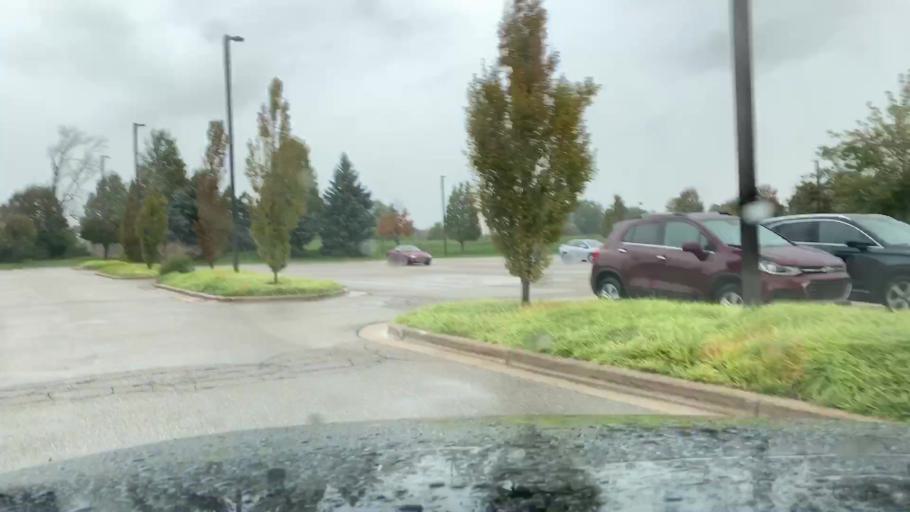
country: US
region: Michigan
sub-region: Ottawa County
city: Holland
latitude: 42.7716
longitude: -86.0713
